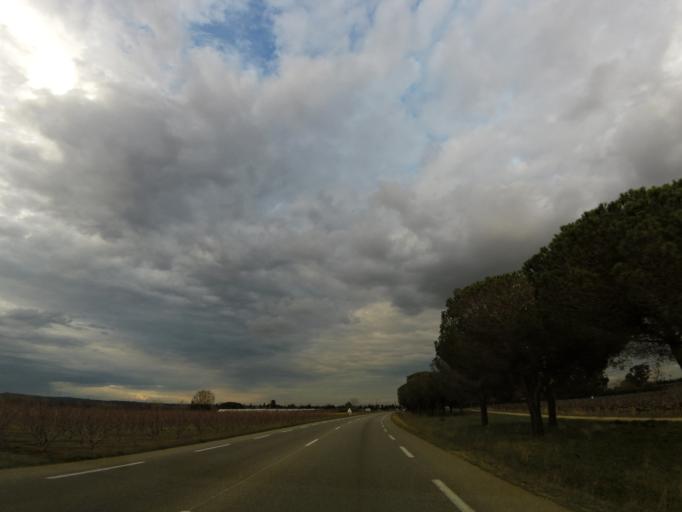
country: FR
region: Languedoc-Roussillon
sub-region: Departement du Gard
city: Vestric-et-Candiac
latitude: 43.7291
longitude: 4.2716
